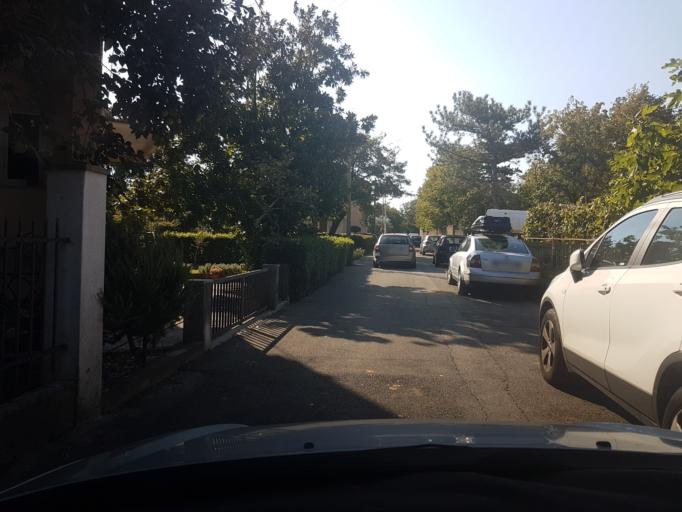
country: IT
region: Friuli Venezia Giulia
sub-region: Provincia di Trieste
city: Sistiana-Visogliano
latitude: 45.7676
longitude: 13.6398
